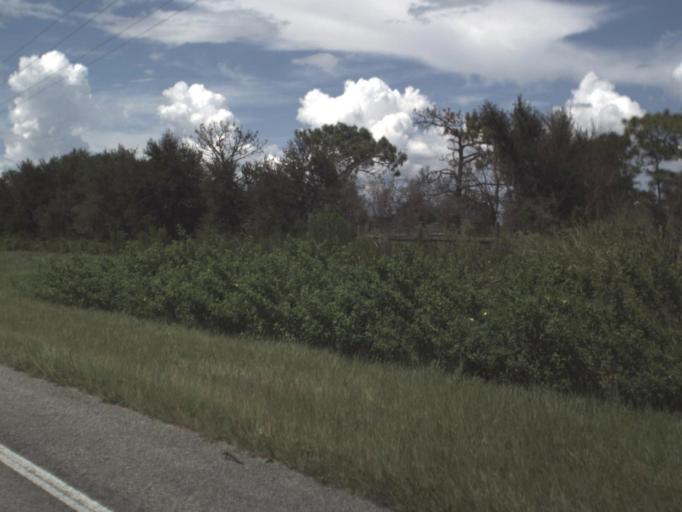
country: US
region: Florida
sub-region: Polk County
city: Babson Park
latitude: 27.8372
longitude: -81.3509
